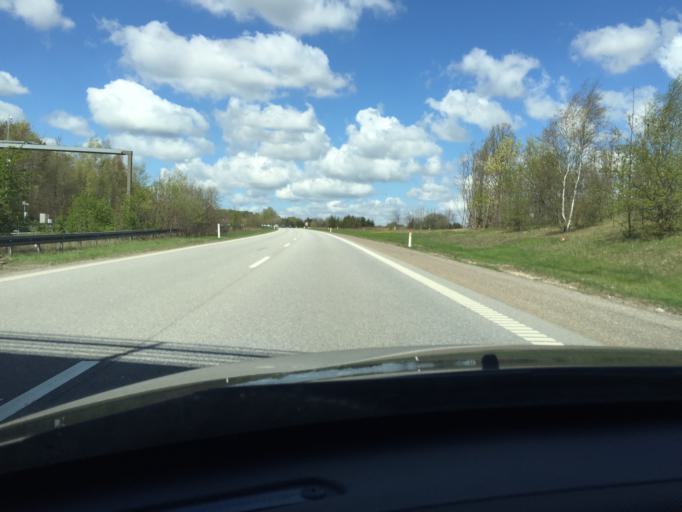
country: DK
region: Capital Region
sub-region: Fureso Kommune
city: Farum
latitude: 55.8244
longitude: 12.3803
